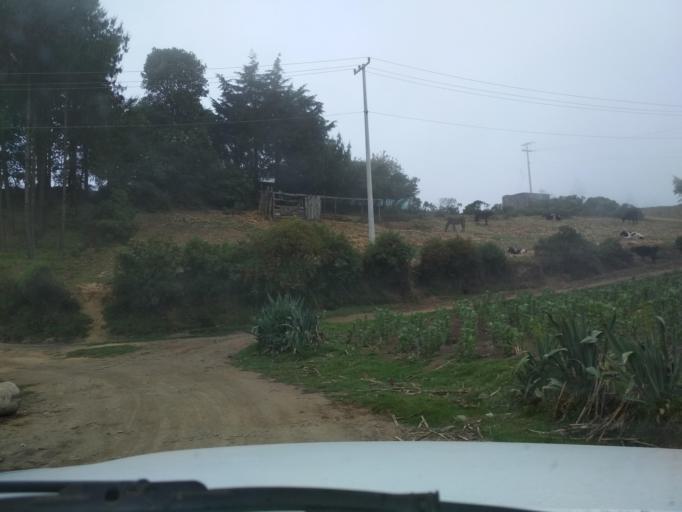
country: MX
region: Veracruz
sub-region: Mariano Escobedo
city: San Isidro el Berro
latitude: 18.9309
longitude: -97.2187
